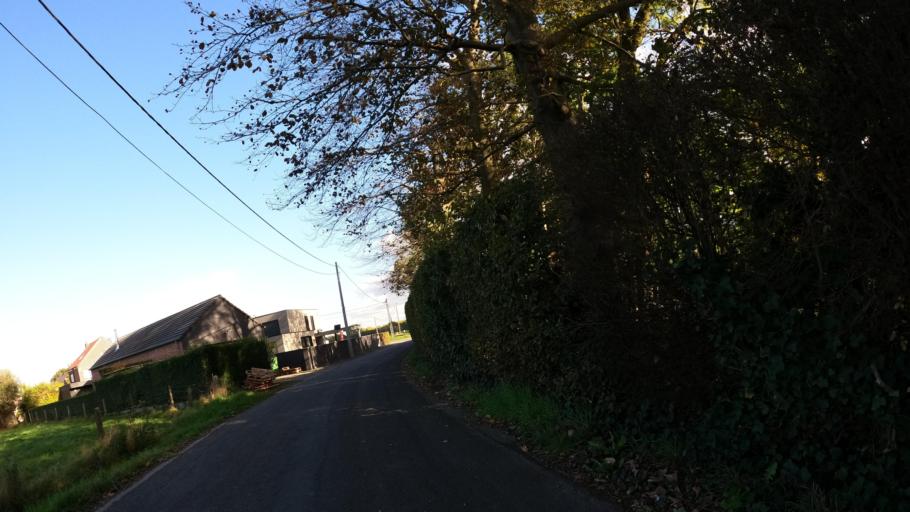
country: BE
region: Flanders
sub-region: Provincie Vlaams-Brabant
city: Opwijk
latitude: 50.9591
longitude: 4.1895
